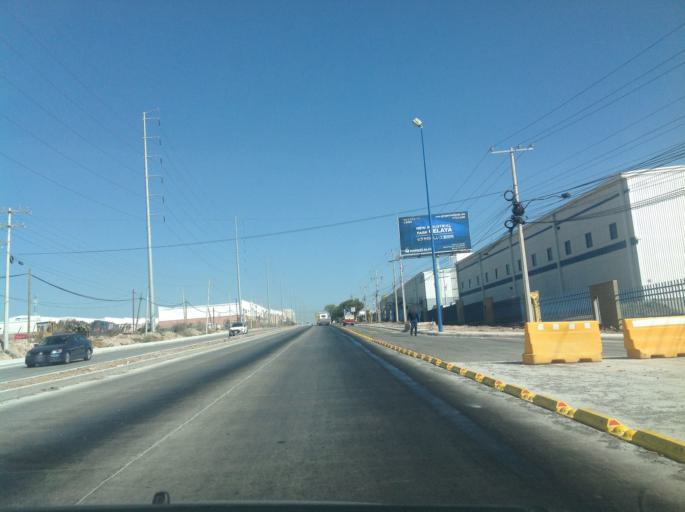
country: MX
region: Queretaro
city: El Colorado
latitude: 20.5567
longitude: -100.2672
